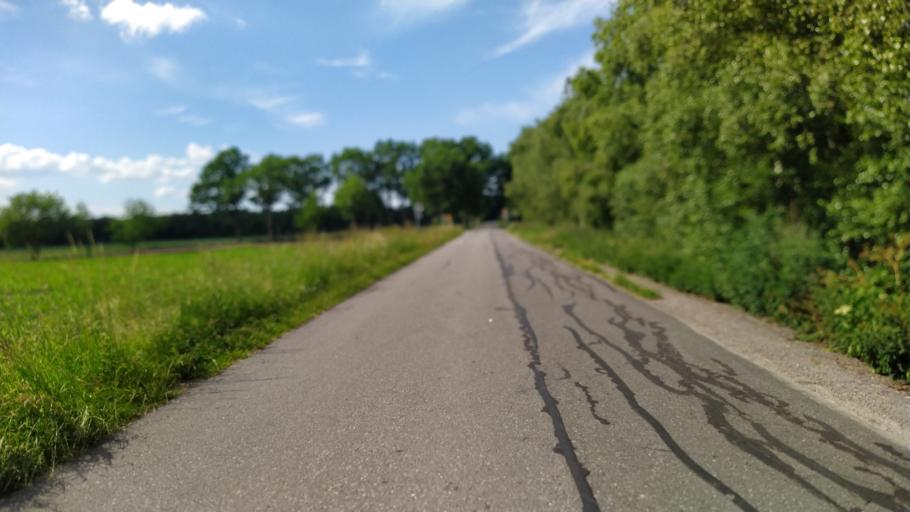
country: DE
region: Lower Saxony
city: Odisheim
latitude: 53.6536
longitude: 8.9367
